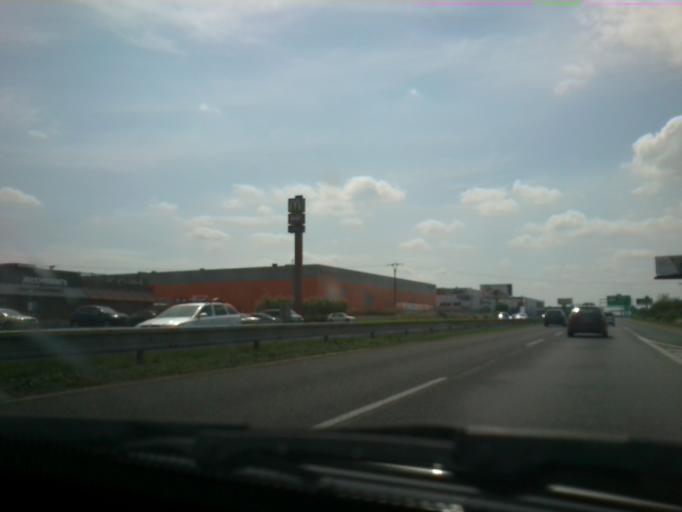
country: CZ
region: Praha
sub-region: Praha 20
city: Horni Pocernice
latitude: 50.1252
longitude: 14.6139
